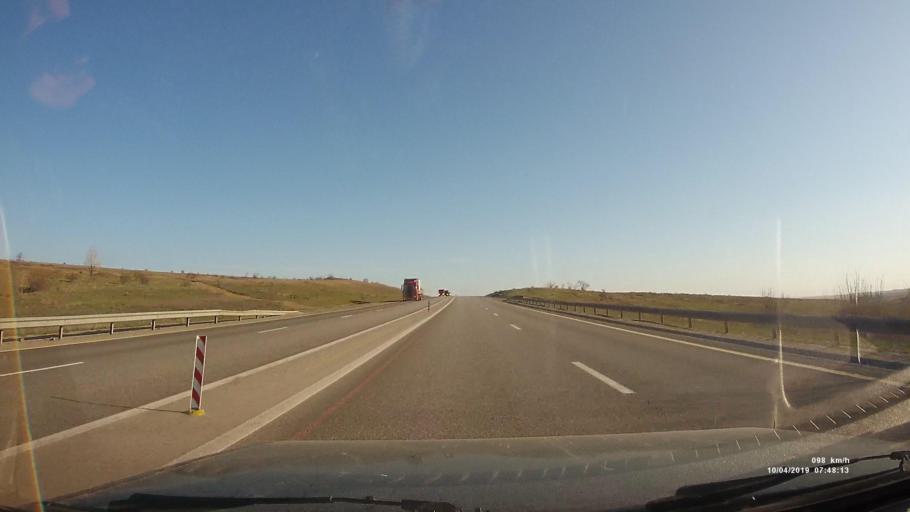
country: RU
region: Rostov
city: Kamensk-Shakhtinskiy
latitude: 48.2309
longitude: 40.2796
